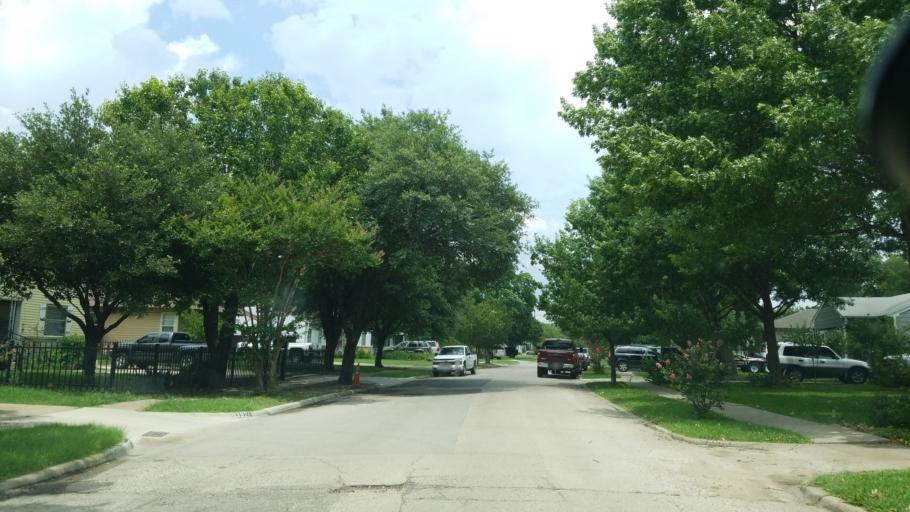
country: US
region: Texas
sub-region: Dallas County
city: Farmers Branch
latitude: 32.8758
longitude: -96.8601
